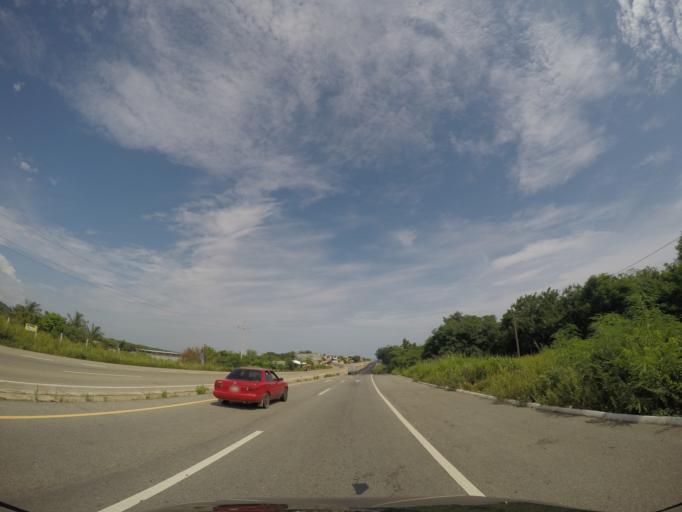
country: MX
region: Oaxaca
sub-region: Santa Maria Colotepec
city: Brisas de Zicatela
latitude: 15.8234
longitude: -97.0175
